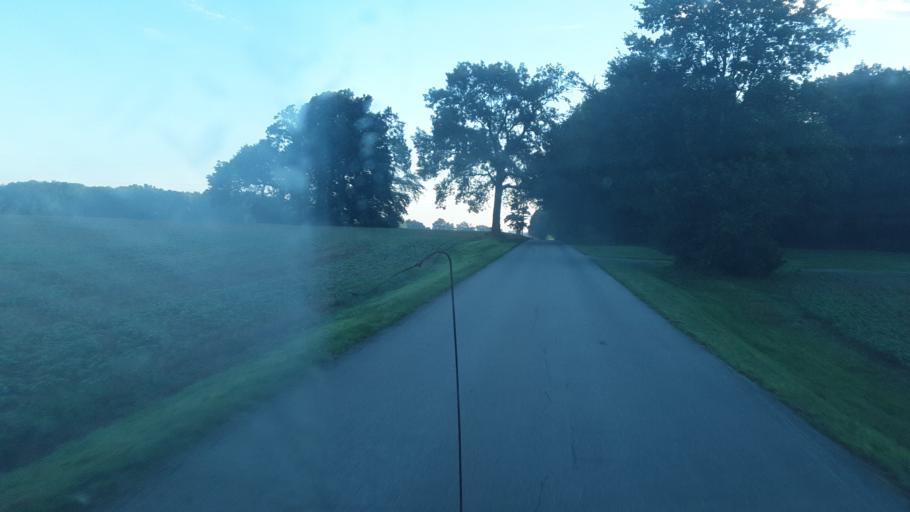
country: US
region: Kentucky
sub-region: Todd County
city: Guthrie
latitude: 36.7145
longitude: -87.1712
